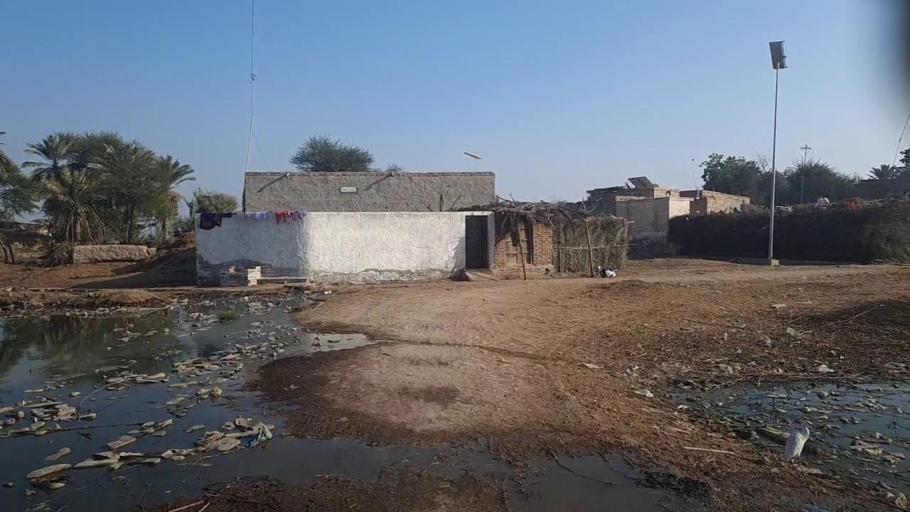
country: PK
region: Sindh
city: Khairpur
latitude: 28.0862
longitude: 69.7156
